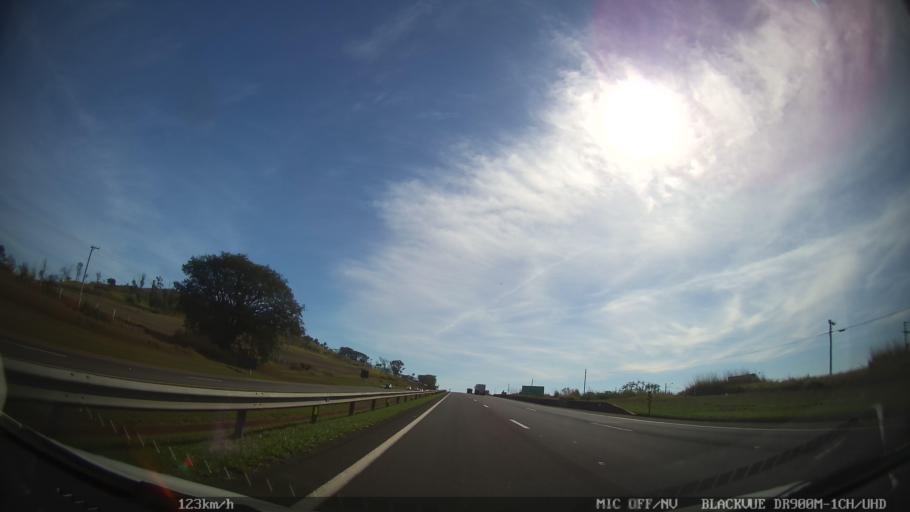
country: BR
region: Sao Paulo
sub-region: Leme
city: Leme
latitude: -22.1612
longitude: -47.3998
